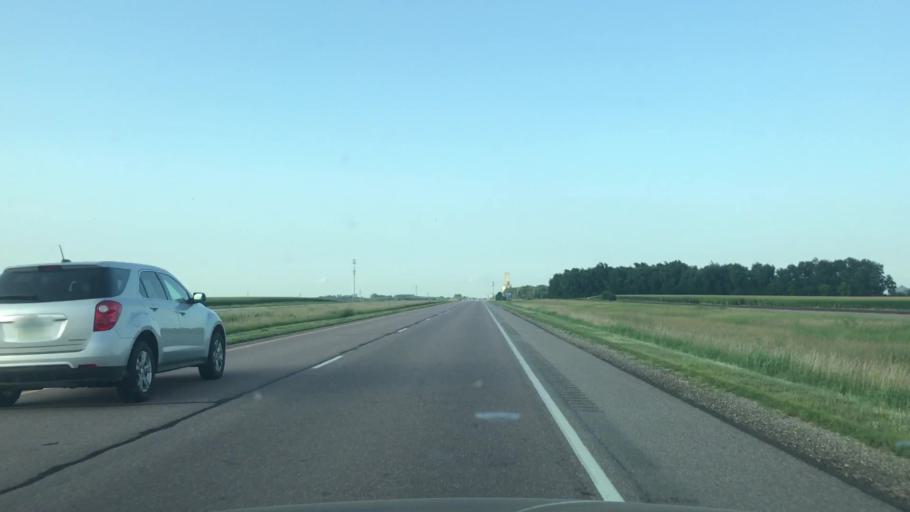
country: US
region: Minnesota
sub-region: Jackson County
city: Lakefield
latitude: 43.7562
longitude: -95.3827
